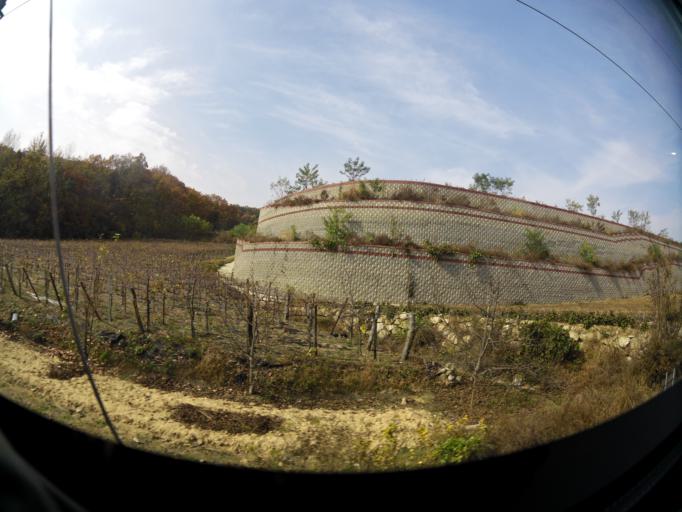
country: KR
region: Gyeongsangbuk-do
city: Gimcheon
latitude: 36.1949
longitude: 128.0051
